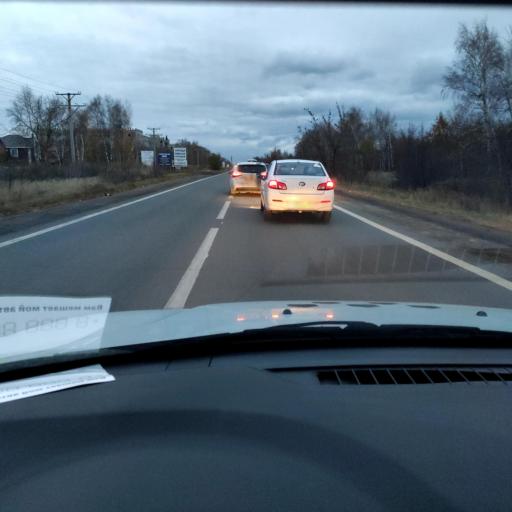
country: RU
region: Samara
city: Tol'yatti
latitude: 53.5534
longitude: 49.3684
